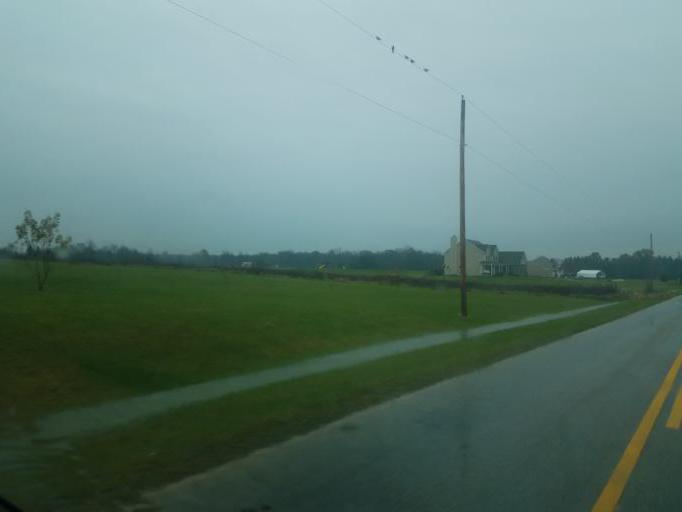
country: US
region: Ohio
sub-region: Knox County
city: Centerburg
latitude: 40.3446
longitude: -82.7933
